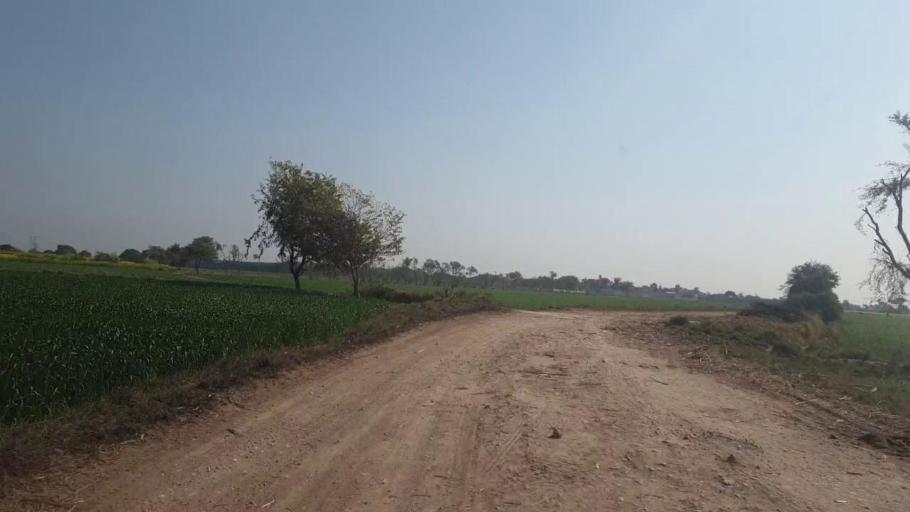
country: PK
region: Sindh
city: Sakrand
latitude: 26.0494
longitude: 68.4534
